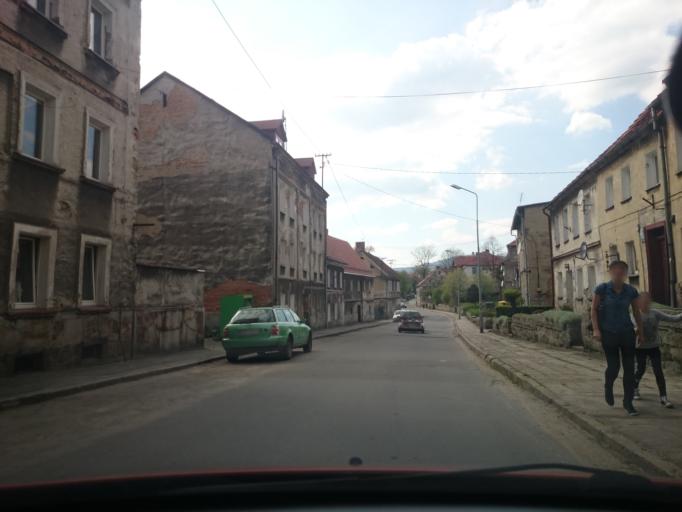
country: PL
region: Lower Silesian Voivodeship
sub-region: Powiat klodzki
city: Bystrzyca Klodzka
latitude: 50.2987
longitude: 16.6464
